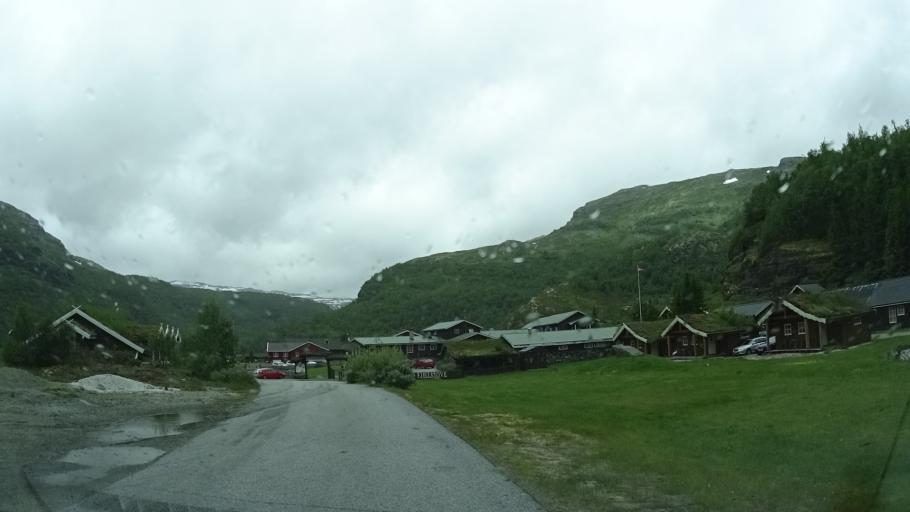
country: NO
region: Sogn og Fjordane
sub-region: Laerdal
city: Laerdalsoyri
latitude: 60.8284
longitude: 7.5076
